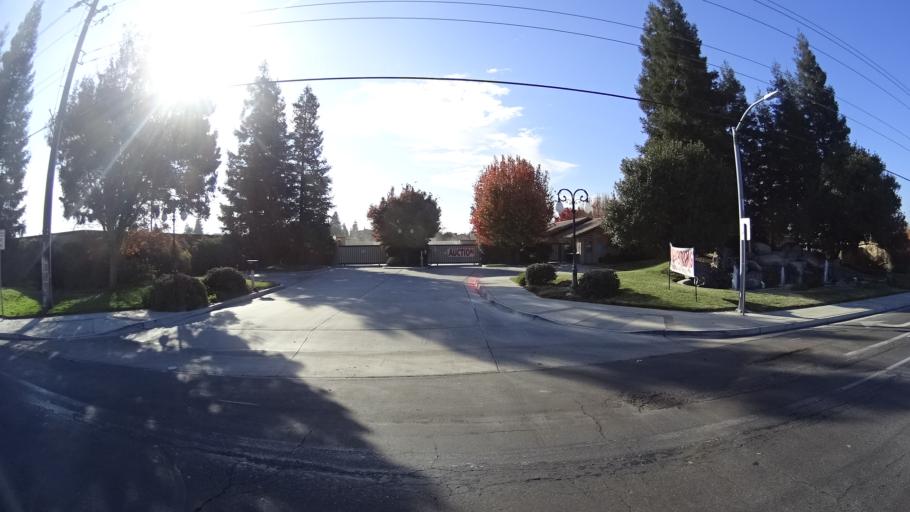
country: US
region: California
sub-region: Kern County
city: Greenacres
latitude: 35.3251
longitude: -119.1118
